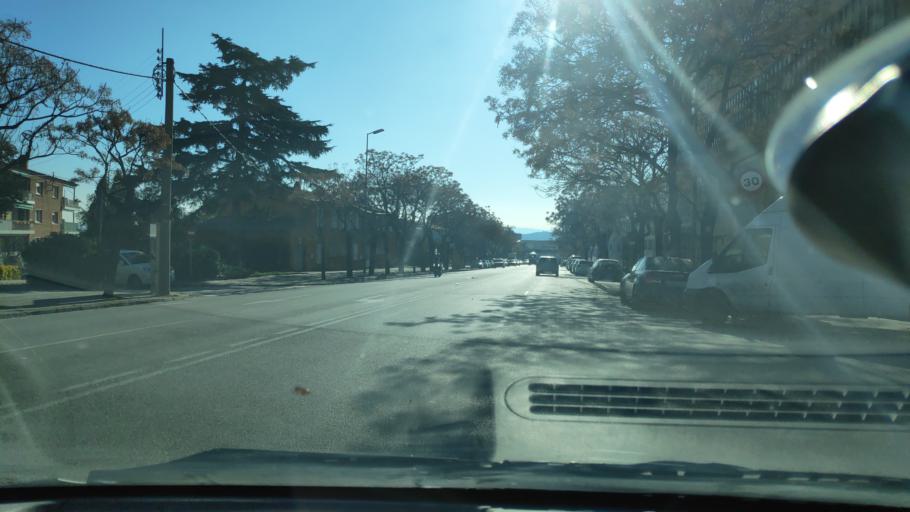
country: ES
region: Catalonia
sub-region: Provincia de Barcelona
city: Sant Quirze del Valles
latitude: 41.5441
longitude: 2.0940
